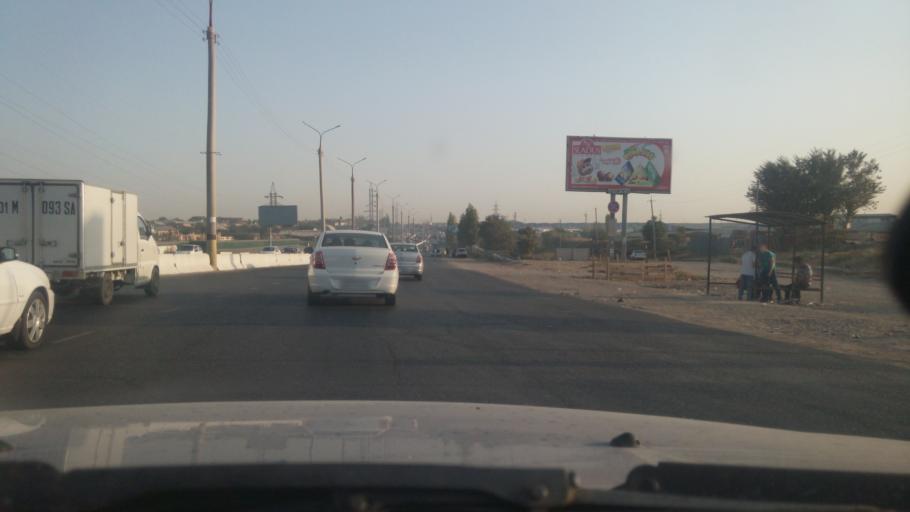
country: UZ
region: Toshkent Shahri
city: Tashkent
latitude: 41.2777
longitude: 69.1467
